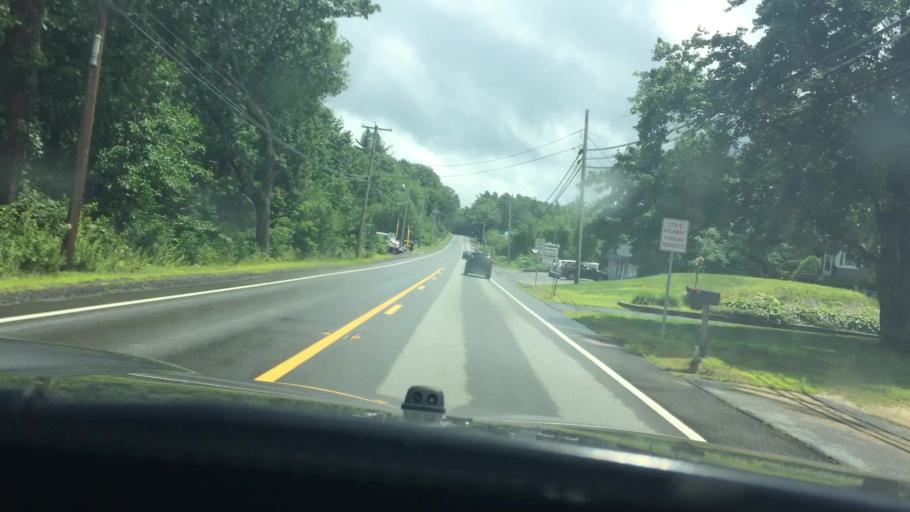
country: US
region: Massachusetts
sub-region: Worcester County
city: Phillipston
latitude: 42.5728
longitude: -72.1608
